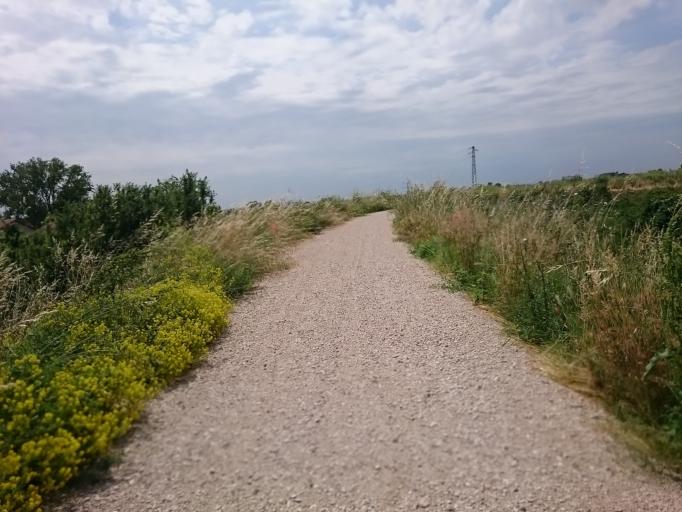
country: IT
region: Veneto
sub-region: Provincia di Padova
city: Carceri
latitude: 45.1915
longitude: 11.6454
